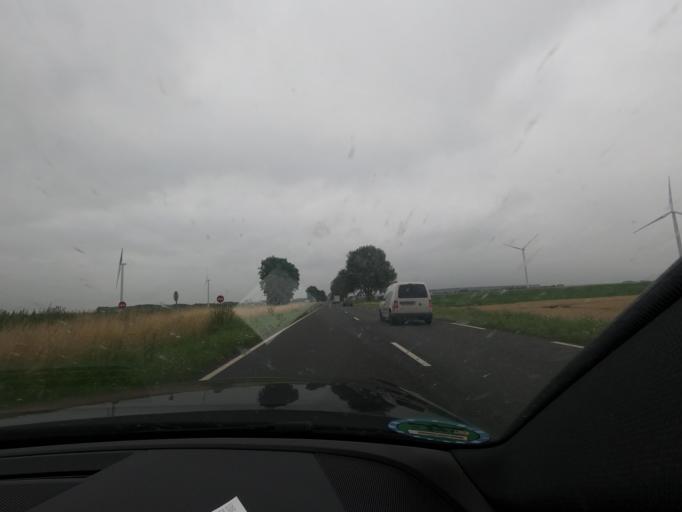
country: FR
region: Picardie
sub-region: Departement de la Somme
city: Roye
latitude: 49.7153
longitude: 2.7489
